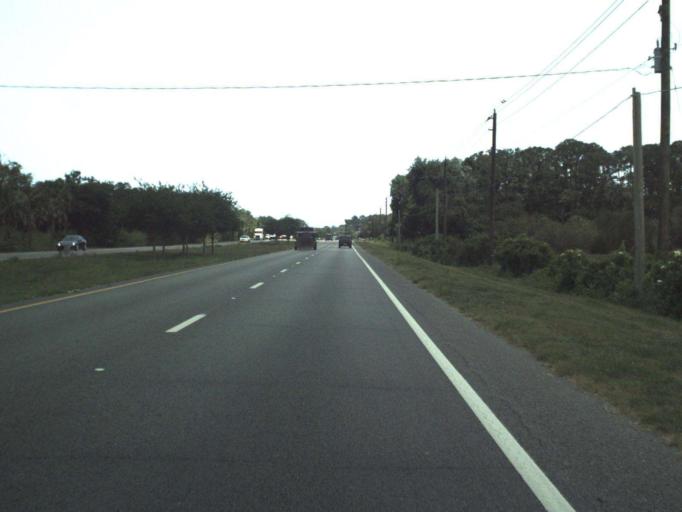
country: US
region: Florida
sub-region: Volusia County
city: Ormond Beach
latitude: 29.2943
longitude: -81.0765
